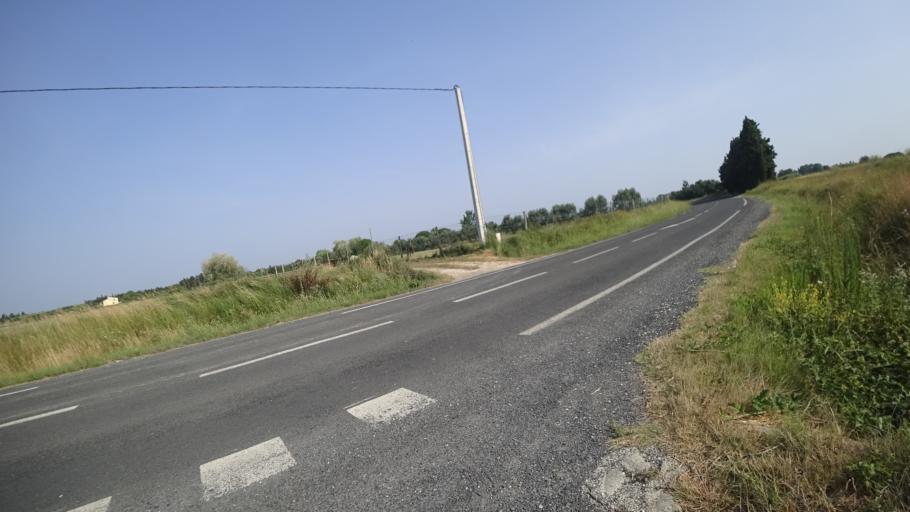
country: FR
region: Languedoc-Roussillon
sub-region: Departement des Pyrenees-Orientales
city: Villelongue-de-la-Salanque
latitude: 42.7332
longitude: 2.9891
